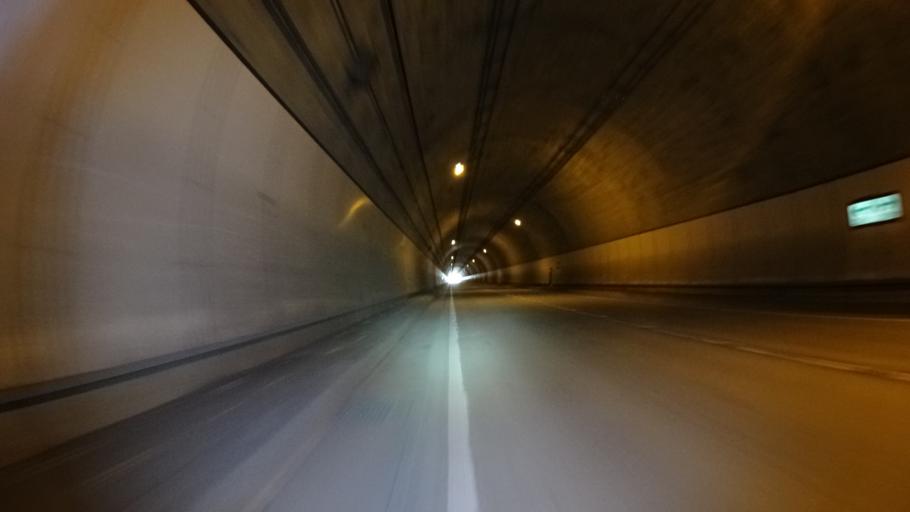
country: JP
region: Yamanashi
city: Uenohara
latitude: 35.6931
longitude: 139.1039
